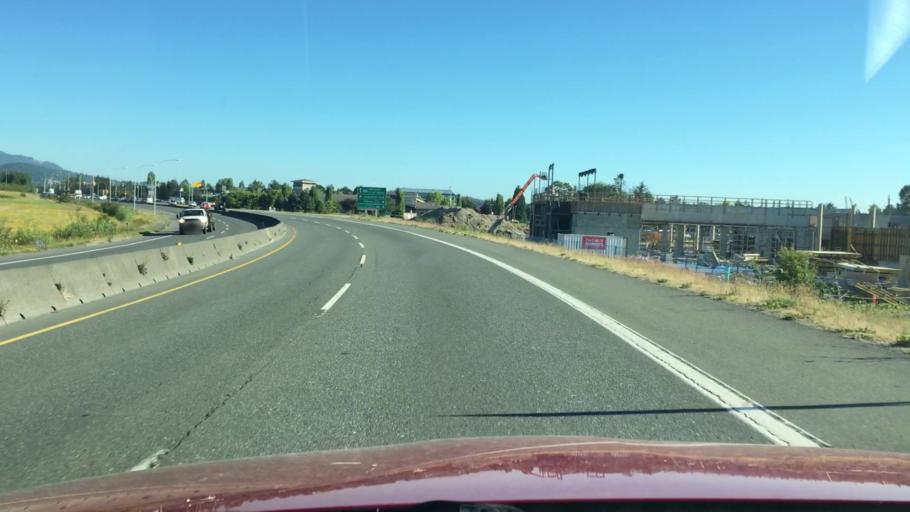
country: CA
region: British Columbia
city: North Saanich
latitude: 48.6455
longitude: -123.4052
